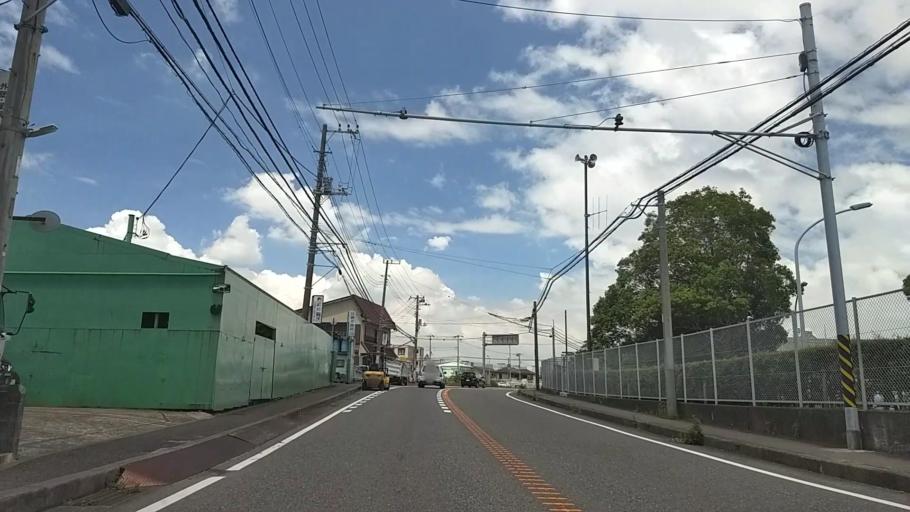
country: JP
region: Kanagawa
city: Fujisawa
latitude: 35.3323
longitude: 139.5096
